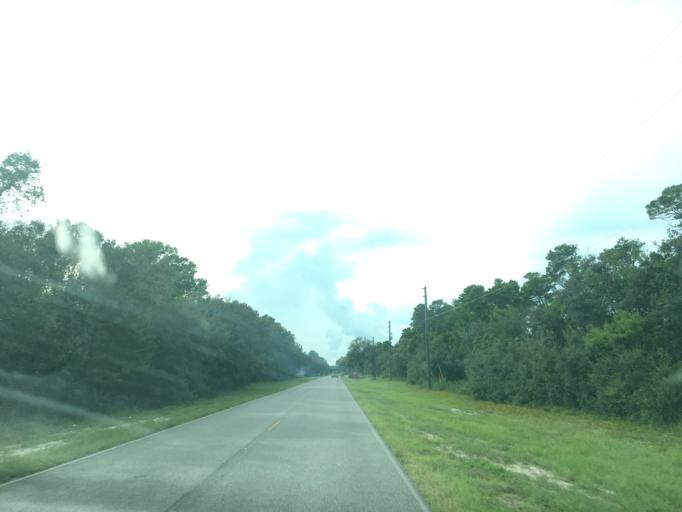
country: US
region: Florida
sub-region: Wakulla County
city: Crawfordville
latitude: 29.9059
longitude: -84.3551
